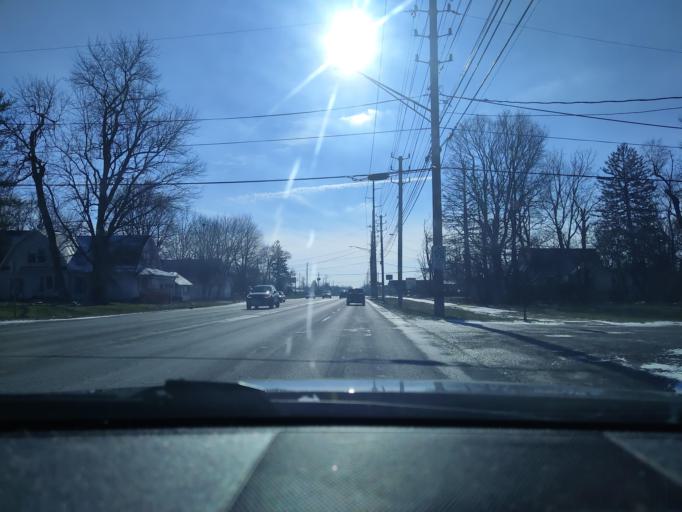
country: US
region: Indiana
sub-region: Marion County
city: Meridian Hills
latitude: 39.8900
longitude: -86.2124
